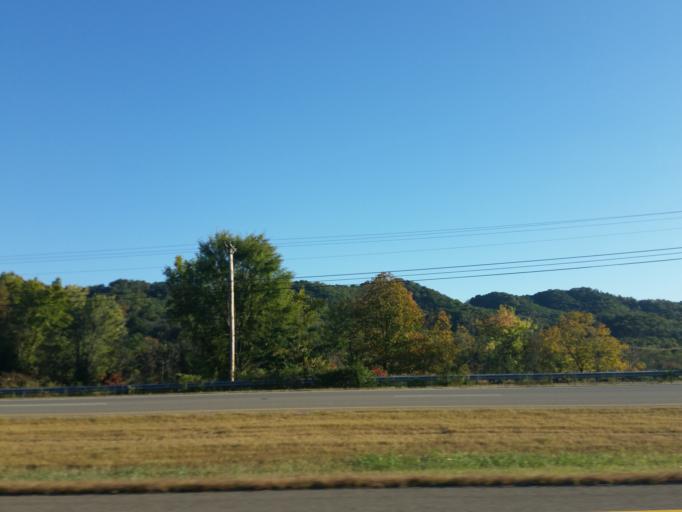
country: US
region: Tennessee
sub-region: Grainger County
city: Bean Station
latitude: 36.3444
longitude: -83.3265
